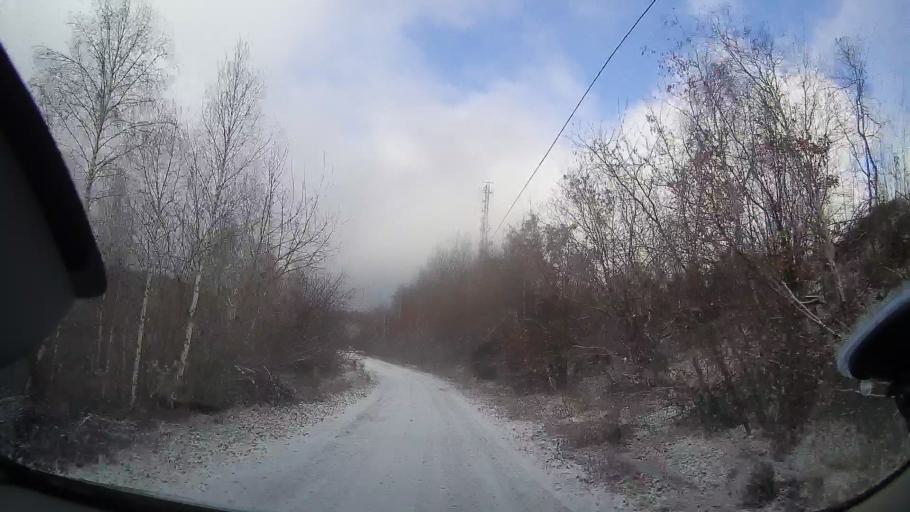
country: RO
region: Cluj
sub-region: Comuna Valea Ierii
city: Valea Ierii
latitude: 46.6543
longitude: 23.3511
